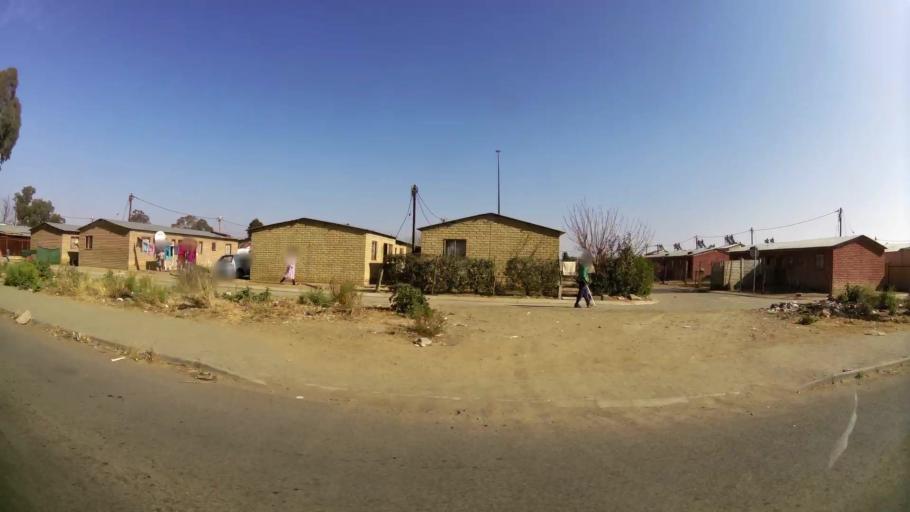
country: ZA
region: Orange Free State
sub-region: Mangaung Metropolitan Municipality
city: Bloemfontein
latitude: -29.1355
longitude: 26.2385
